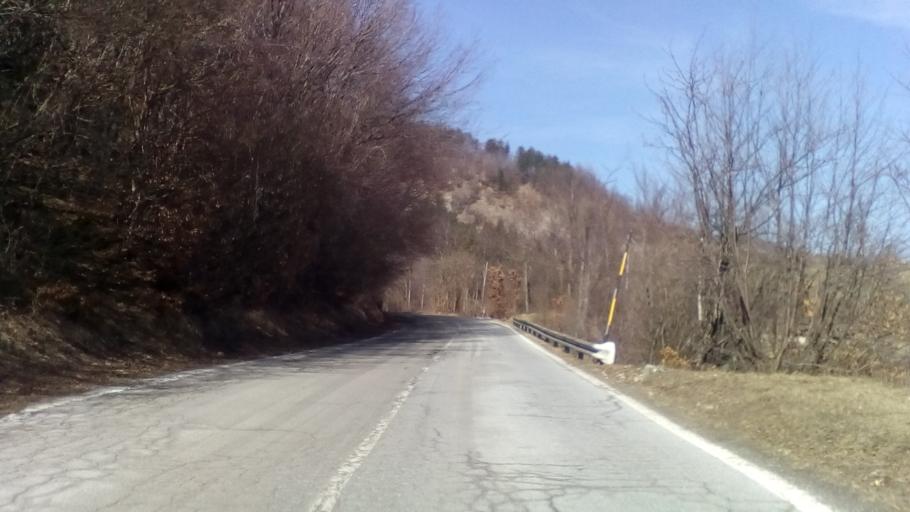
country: IT
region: Emilia-Romagna
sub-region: Provincia di Modena
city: Pievepelago
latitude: 44.2235
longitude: 10.6287
